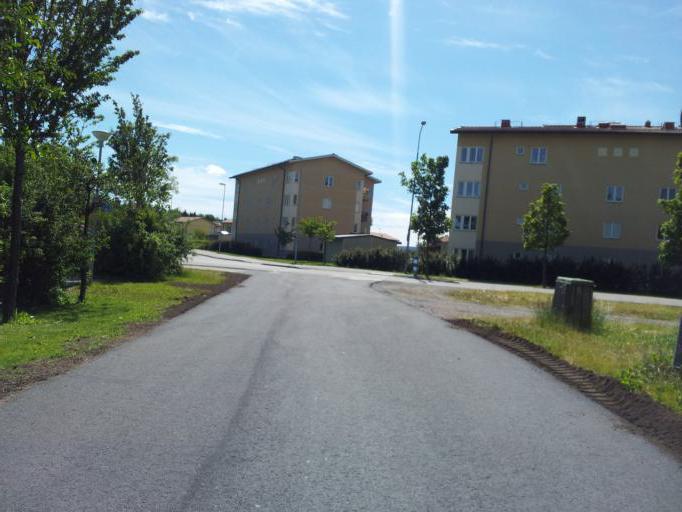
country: SE
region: Uppsala
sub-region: Uppsala Kommun
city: Saevja
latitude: 59.8591
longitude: 17.7047
